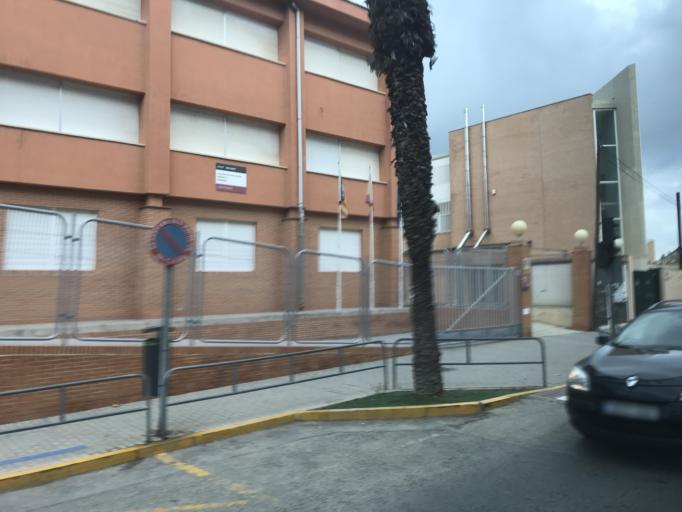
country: ES
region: Valencia
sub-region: Provincia de Alicante
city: Guardamar del Segura
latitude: 38.0866
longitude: -0.6554
